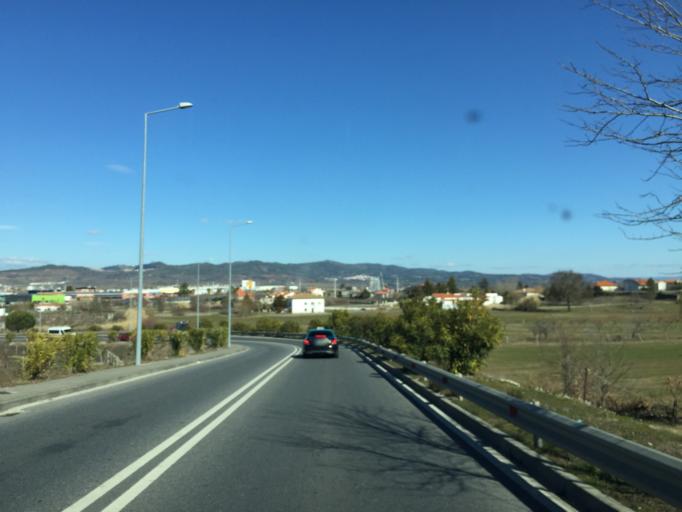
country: PT
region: Castelo Branco
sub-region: Concelho do Fundao
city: Fundao
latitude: 40.1615
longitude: -7.4970
